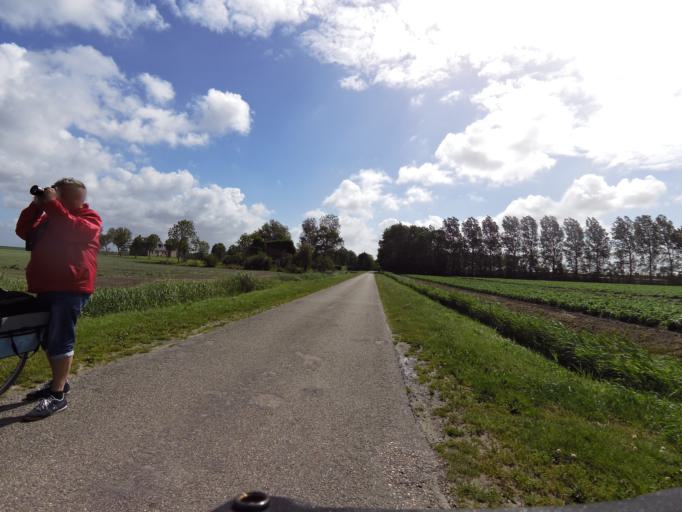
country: NL
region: South Holland
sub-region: Gemeente Goeree-Overflakkee
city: Goedereede
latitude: 51.7024
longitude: 3.9727
